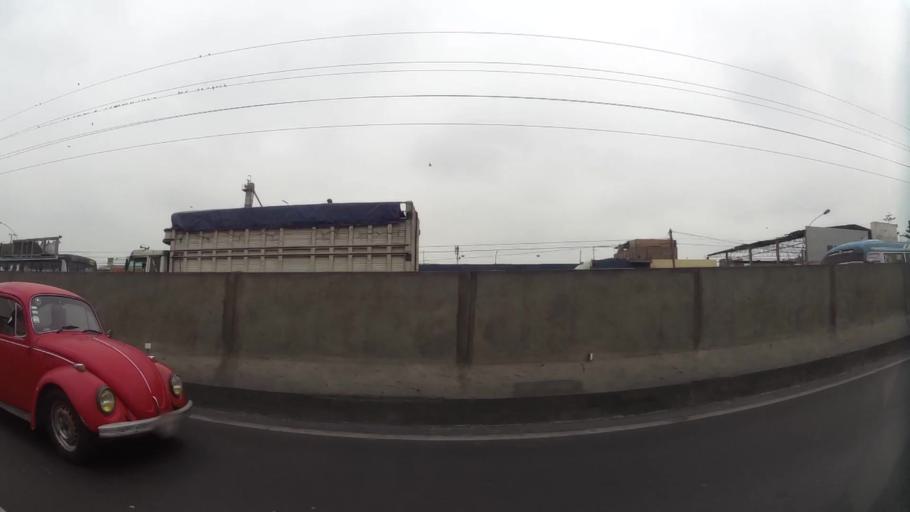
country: PE
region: Lima
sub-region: Lima
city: Independencia
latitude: -11.9562
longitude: -77.0694
